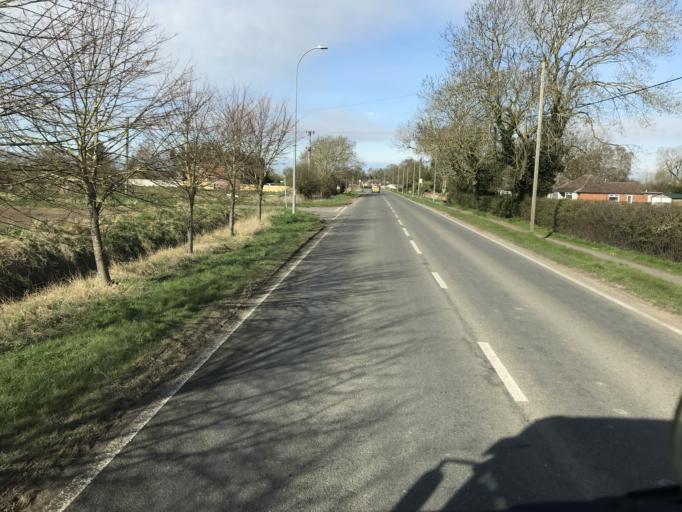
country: GB
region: England
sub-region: Lincolnshire
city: Market Rasen
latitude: 53.3883
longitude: -0.3471
